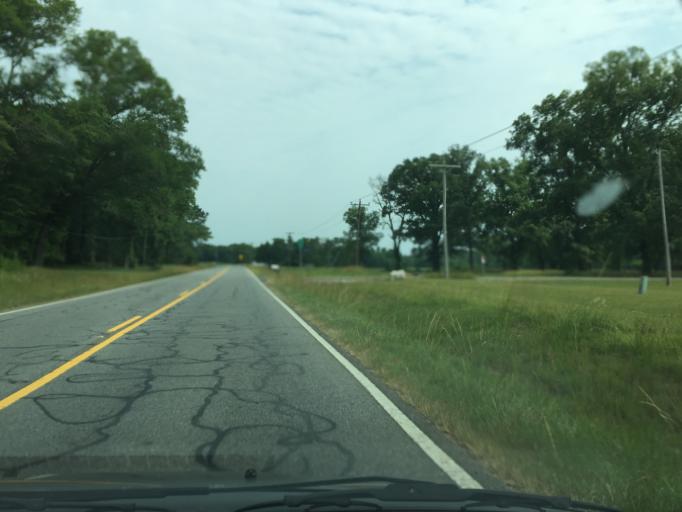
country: US
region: Georgia
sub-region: Catoosa County
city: Ringgold
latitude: 34.8518
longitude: -85.1426
